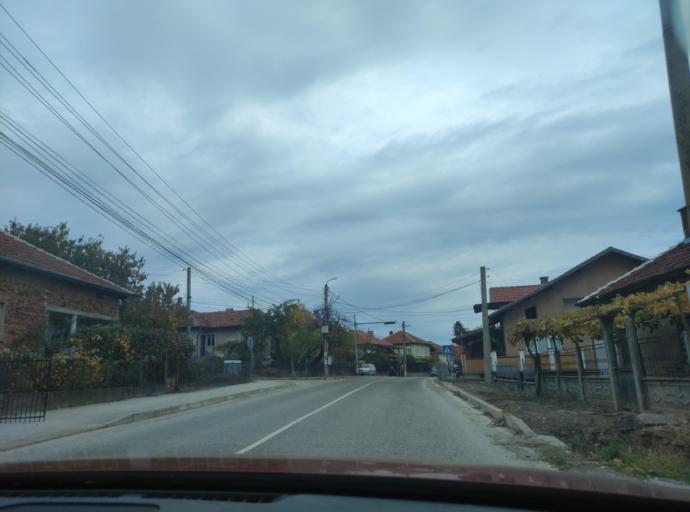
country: BG
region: Montana
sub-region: Obshtina Berkovitsa
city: Berkovitsa
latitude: 43.2047
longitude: 23.1605
